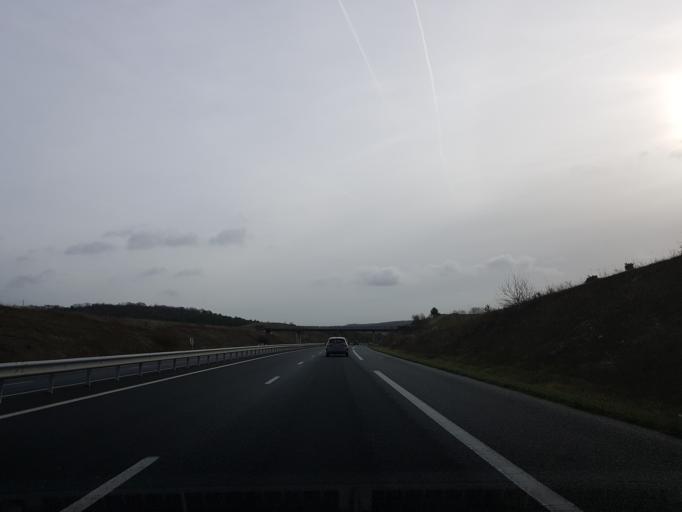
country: FR
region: Bourgogne
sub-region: Departement de l'Yonne
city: Soucy
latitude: 48.2572
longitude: 3.3311
